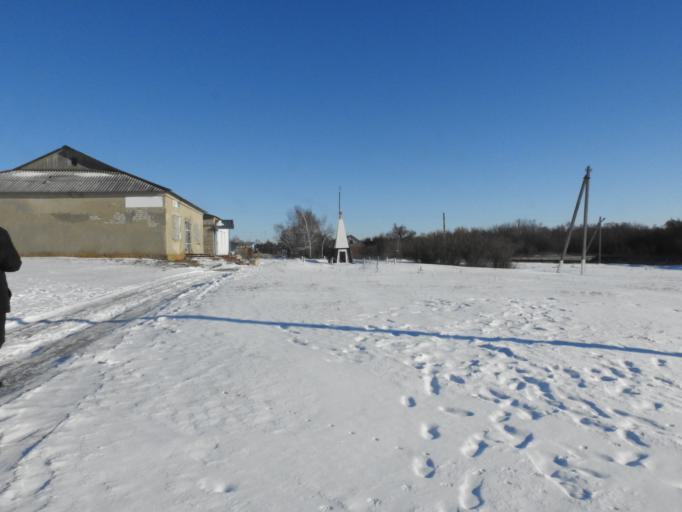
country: RU
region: Saratov
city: Lysyye Gory
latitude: 51.4307
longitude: 44.9329
